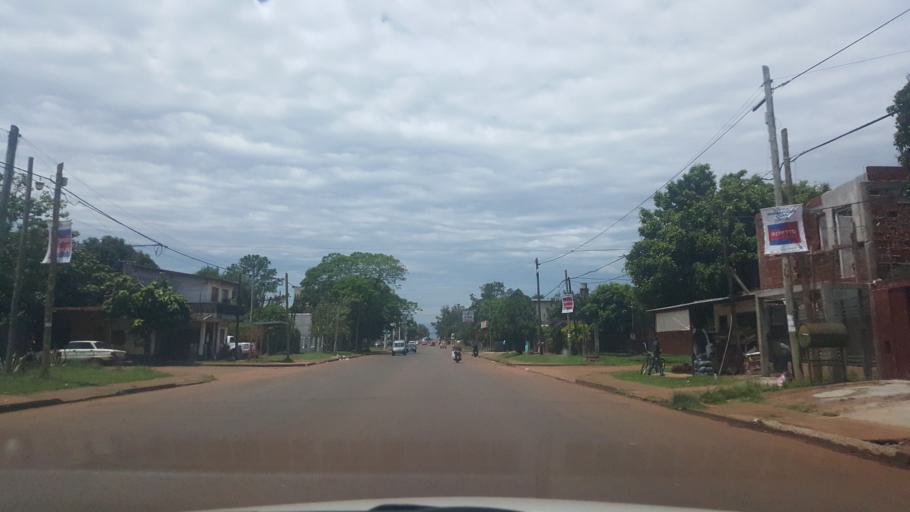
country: AR
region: Misiones
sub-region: Departamento de Capital
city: Posadas
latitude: -27.3786
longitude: -55.9207
